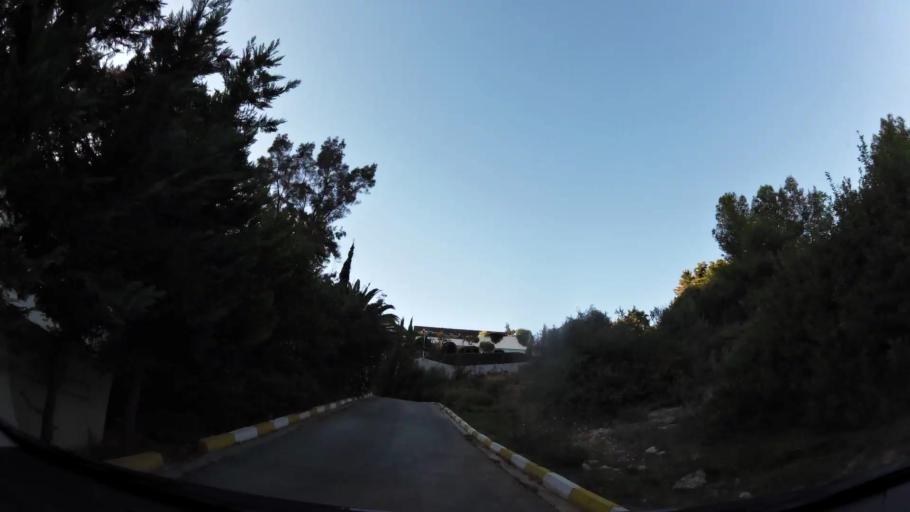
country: GR
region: Attica
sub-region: Nomarchia Anatolikis Attikis
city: Vari
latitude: 37.8236
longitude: 23.7942
